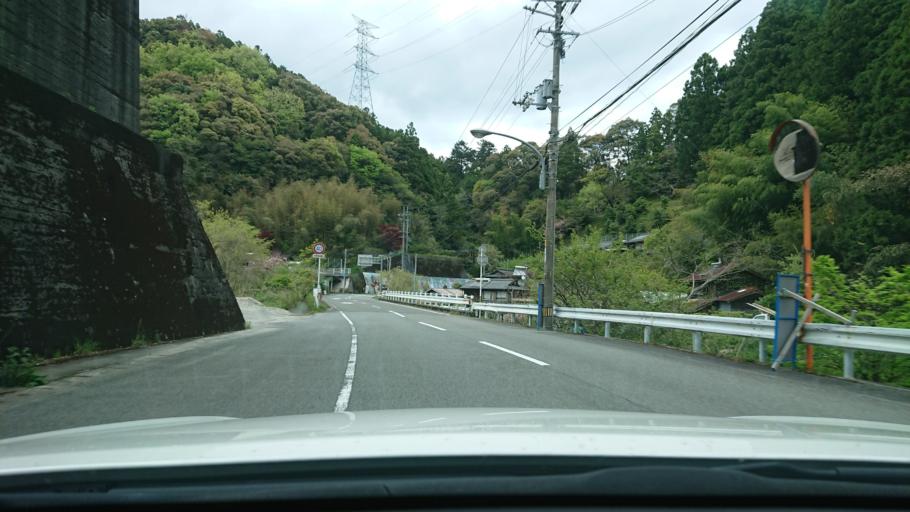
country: JP
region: Tokushima
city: Ishii
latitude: 33.9146
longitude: 134.4214
